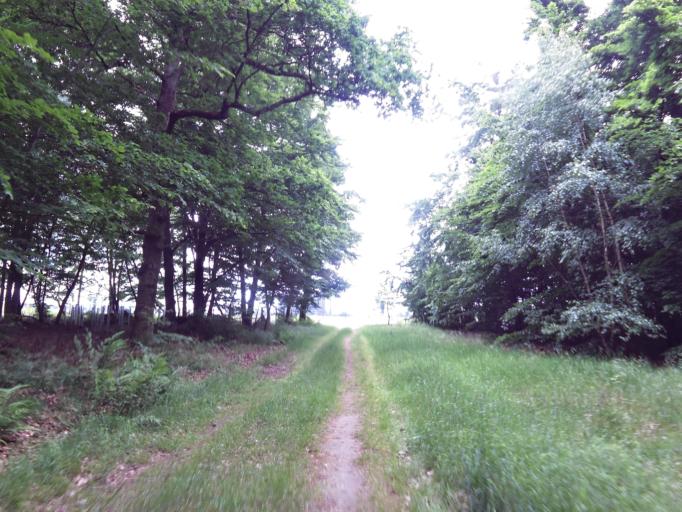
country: DE
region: Hesse
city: Morfelden-Walldorf
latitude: 50.0220
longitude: 8.5655
